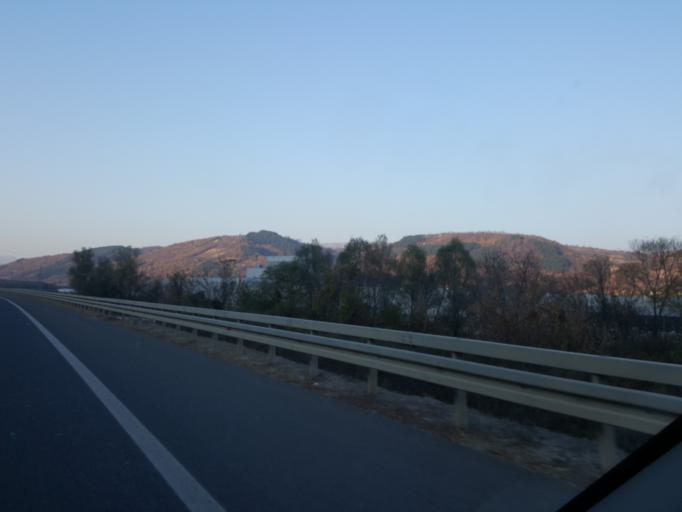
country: RS
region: Central Serbia
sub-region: Pirotski Okrug
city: Pirot
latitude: 43.1704
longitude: 22.5738
